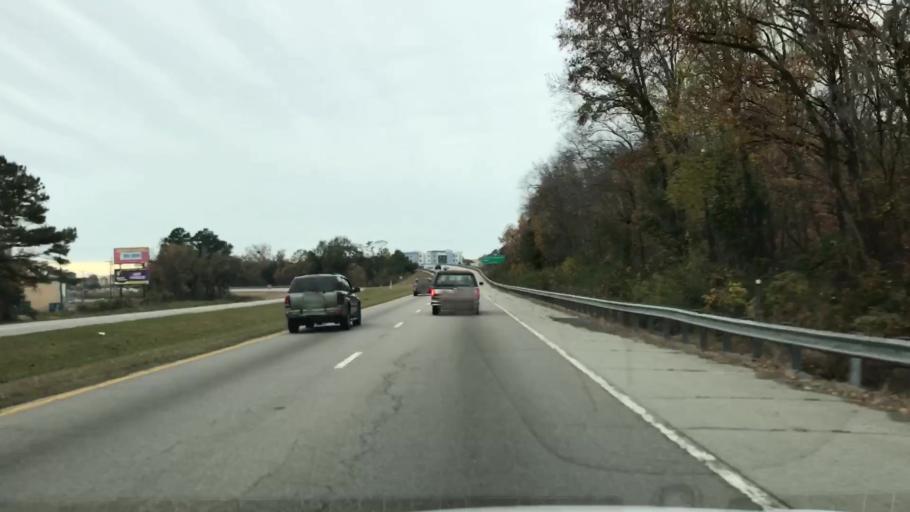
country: US
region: South Carolina
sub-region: Berkeley County
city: Hanahan
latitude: 32.9441
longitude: -80.0479
